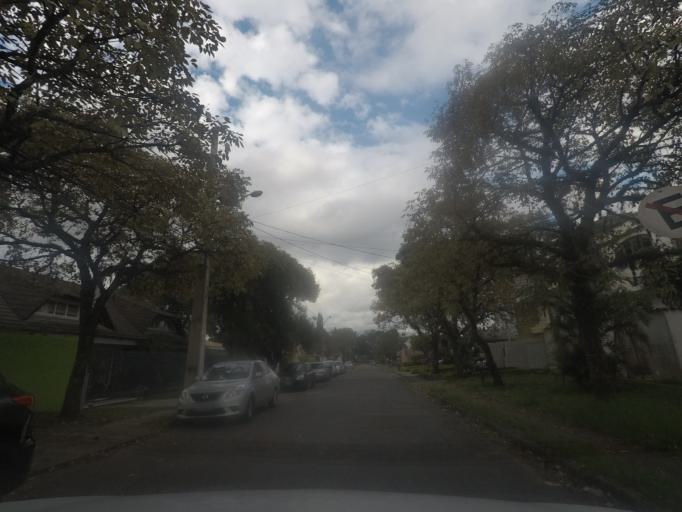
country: BR
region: Parana
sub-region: Pinhais
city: Pinhais
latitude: -25.4576
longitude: -49.2248
